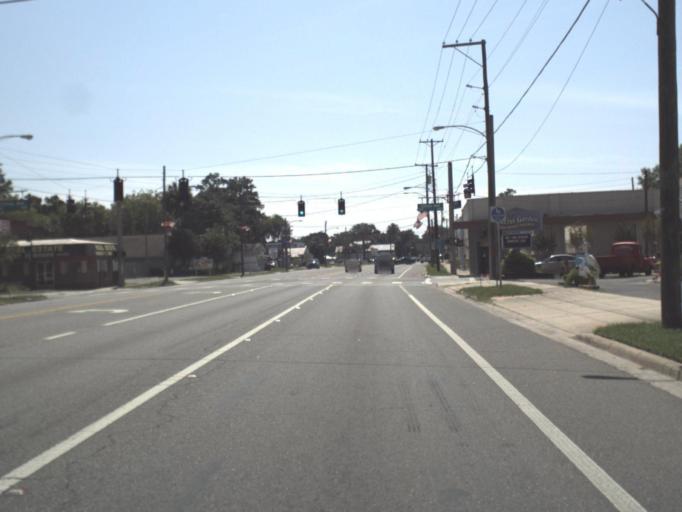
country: US
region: Florida
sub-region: Citrus County
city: Crystal River
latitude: 28.8998
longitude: -82.5924
